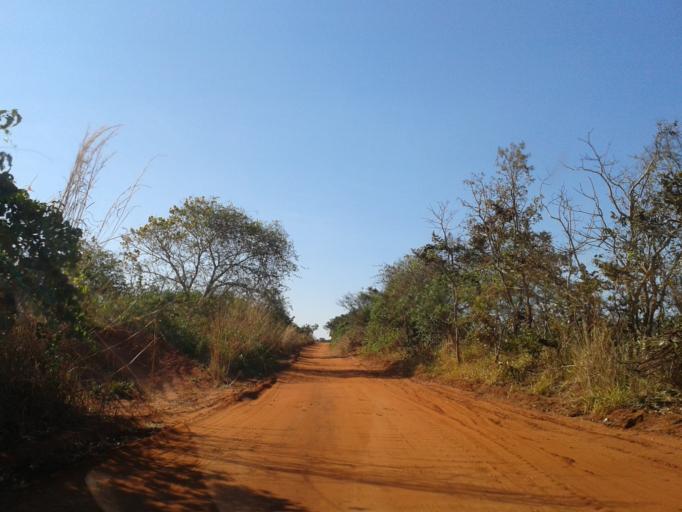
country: BR
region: Minas Gerais
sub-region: Ituiutaba
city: Ituiutaba
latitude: -19.0177
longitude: -49.3571
